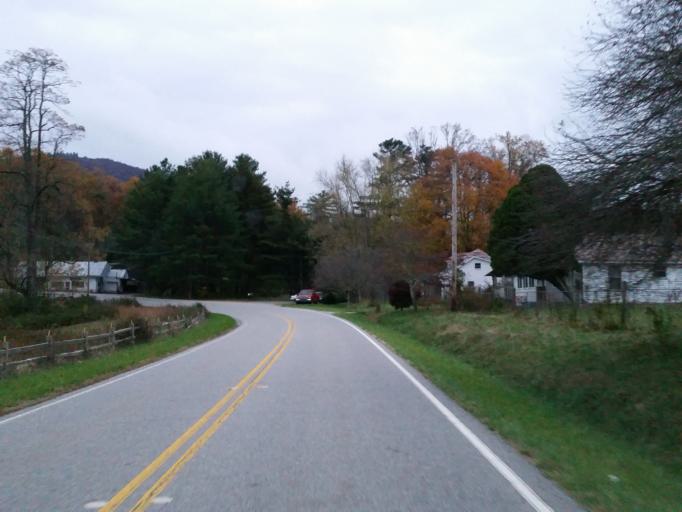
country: US
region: Georgia
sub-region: Lumpkin County
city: Dahlonega
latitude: 34.6840
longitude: -84.0191
